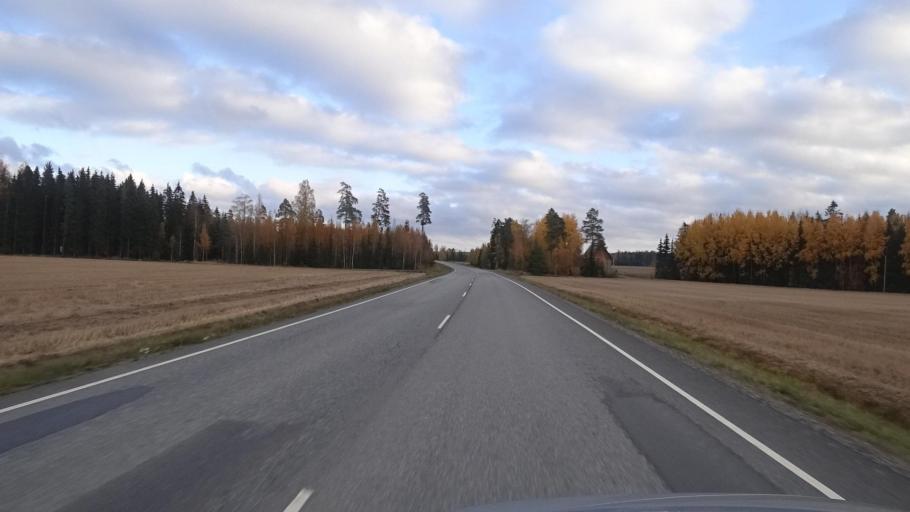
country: FI
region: Varsinais-Suomi
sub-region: Loimaa
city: Alastaro
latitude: 60.9122
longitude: 22.9080
